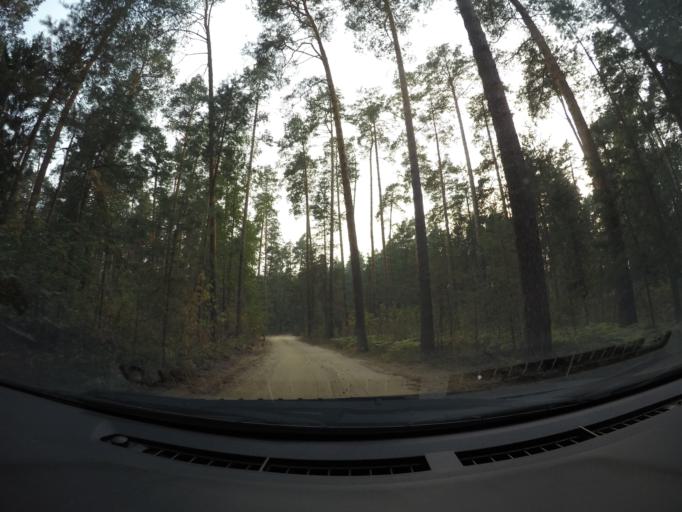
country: RU
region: Moskovskaya
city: Imeni Tsyurupy
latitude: 55.5028
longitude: 38.6907
